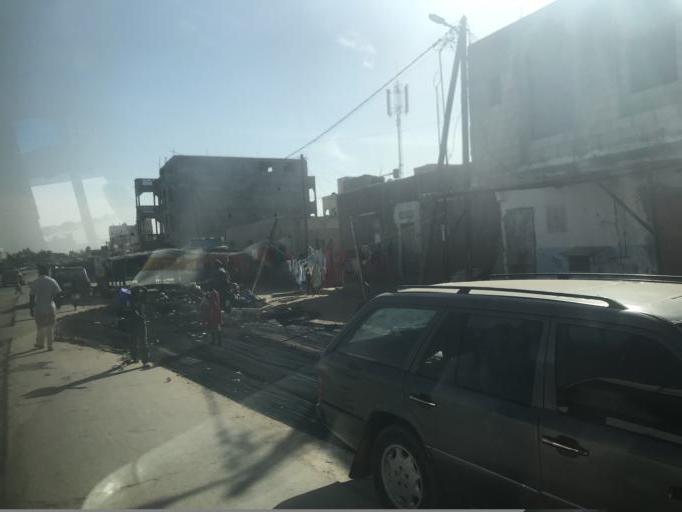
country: SN
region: Saint-Louis
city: Saint-Louis
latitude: 16.0440
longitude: -16.5055
